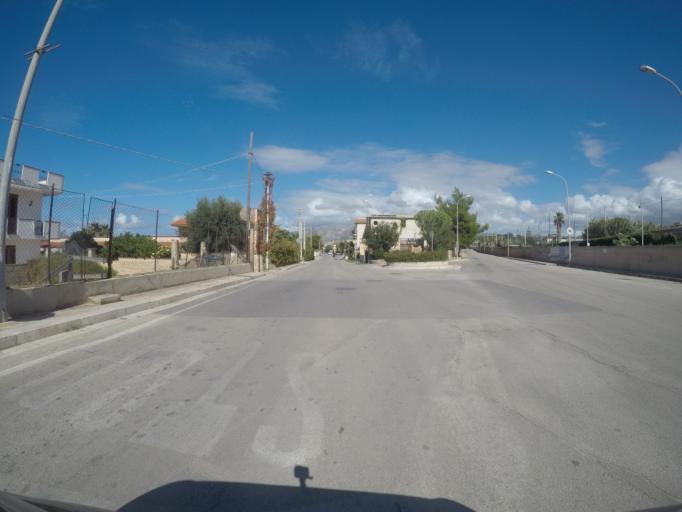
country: IT
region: Sicily
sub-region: Palermo
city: Trappeto
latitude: 38.0641
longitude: 13.0334
